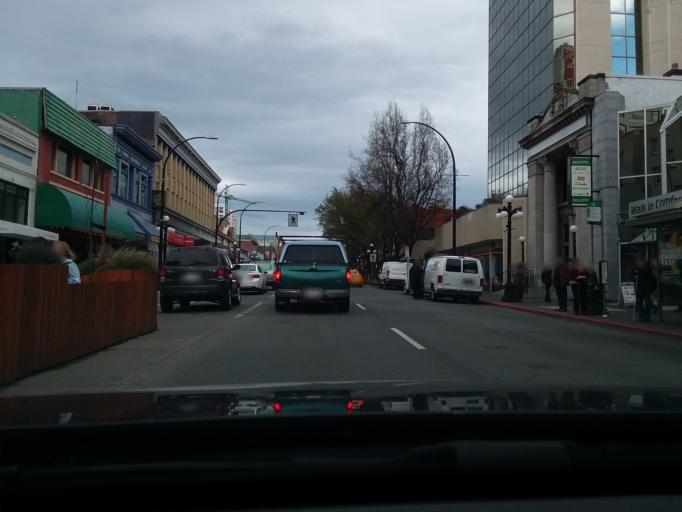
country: CA
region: British Columbia
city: Victoria
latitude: 48.4246
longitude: -123.3647
